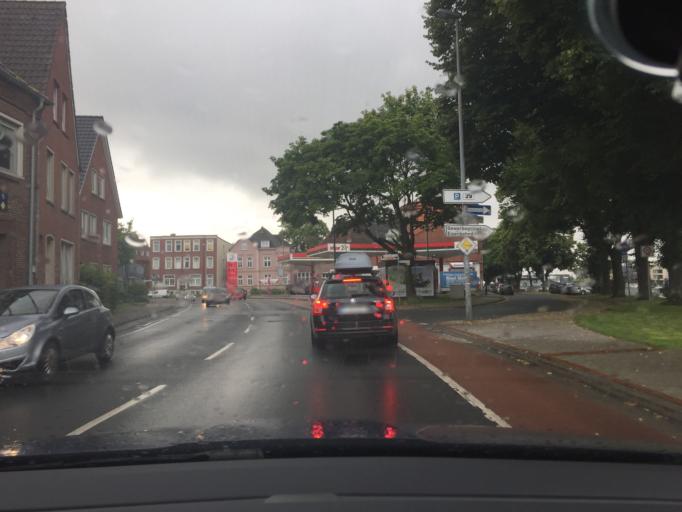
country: DE
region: Lower Saxony
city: Emden
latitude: 53.3652
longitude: 7.2097
